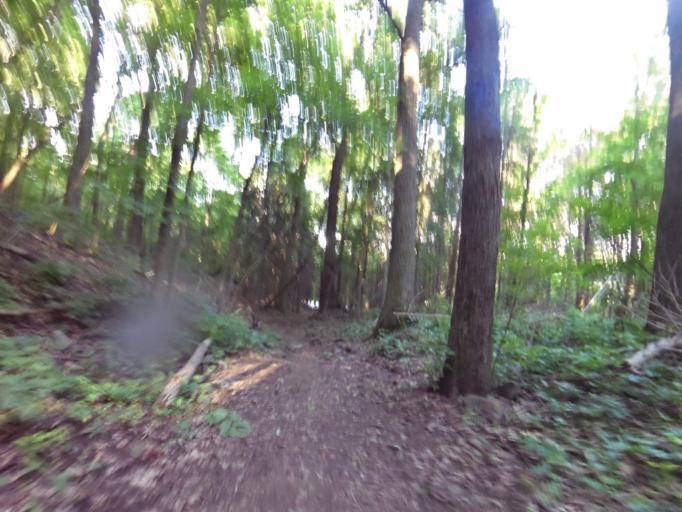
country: CA
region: Quebec
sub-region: Montreal
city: Montreal
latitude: 45.5001
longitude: -73.5907
